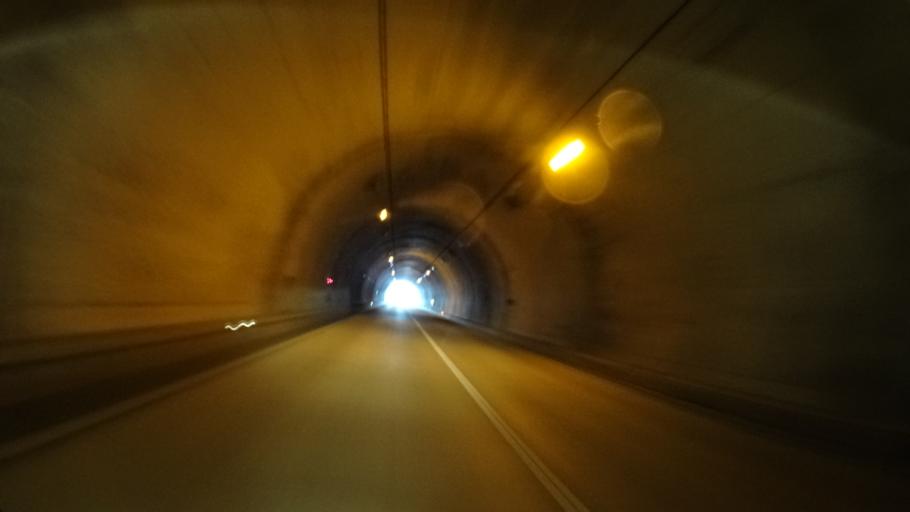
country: JP
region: Fukui
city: Maruoka
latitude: 36.1851
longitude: 136.3418
